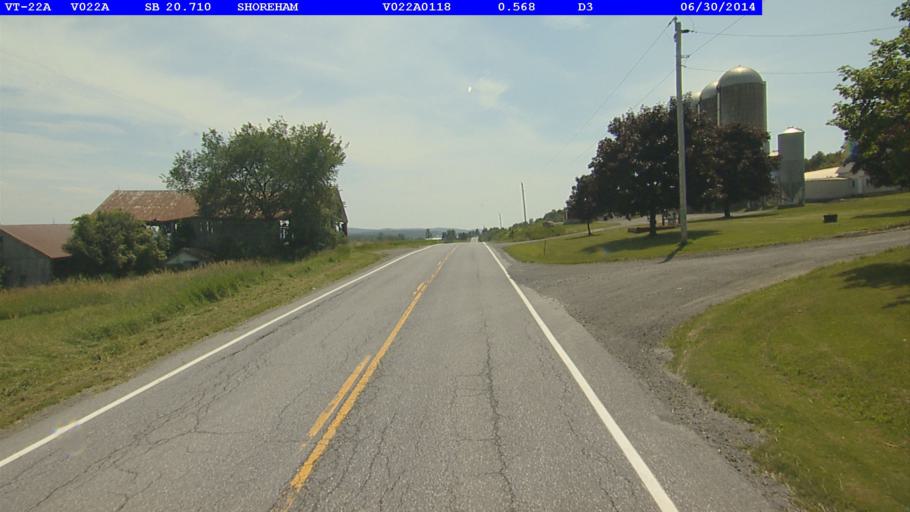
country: US
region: New York
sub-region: Essex County
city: Ticonderoga
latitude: 43.8575
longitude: -73.3093
